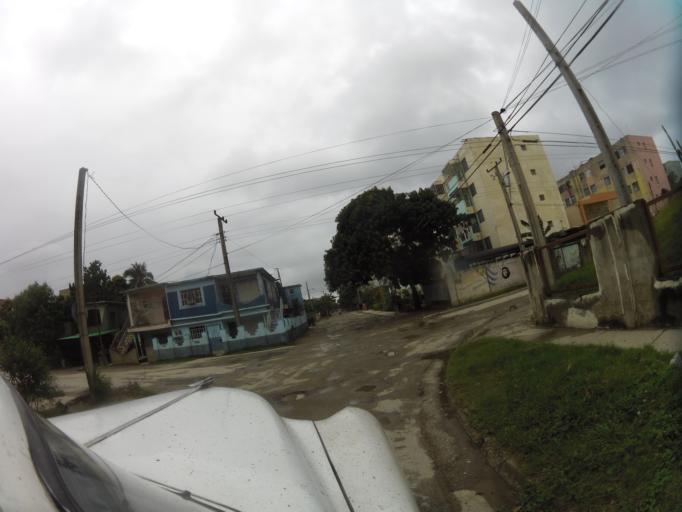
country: CU
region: Las Tunas
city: Las Tunas
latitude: 20.9667
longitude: -76.9362
